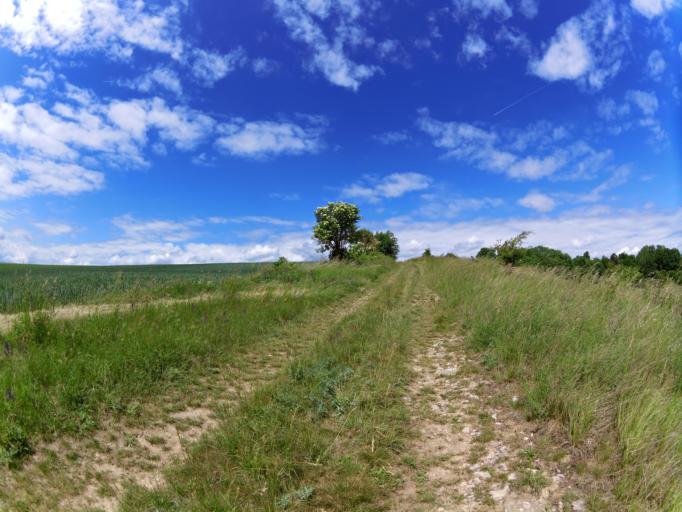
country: DE
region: Bavaria
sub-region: Regierungsbezirk Unterfranken
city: Sommerhausen
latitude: 49.6703
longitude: 10.0134
